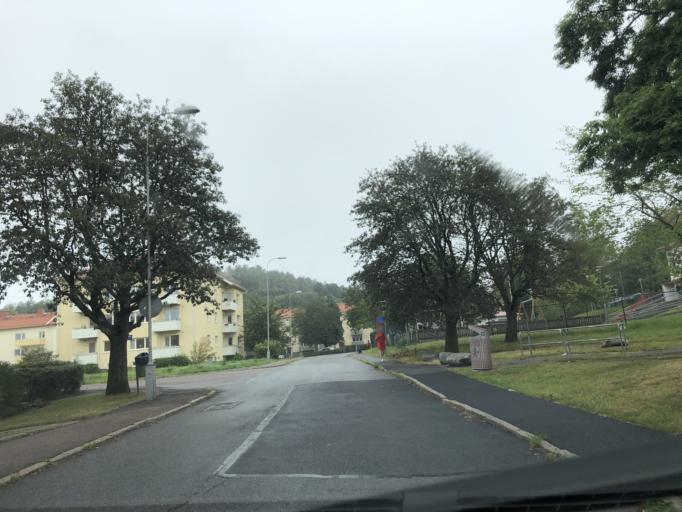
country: SE
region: Vaestra Goetaland
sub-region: Goteborg
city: Majorna
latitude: 57.7291
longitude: 11.9326
